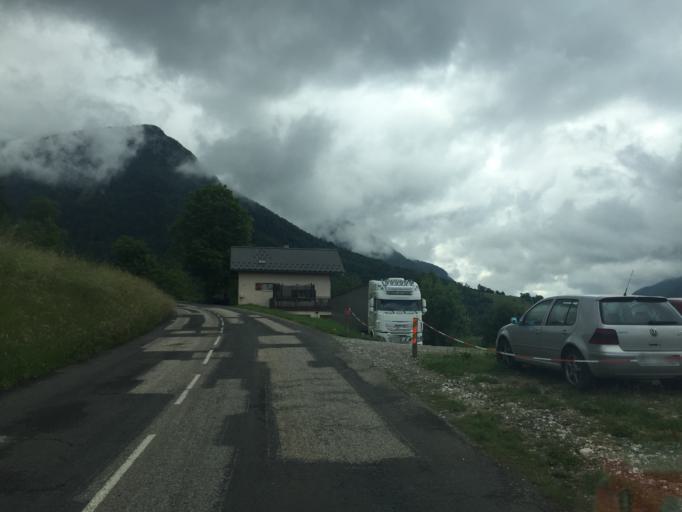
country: FR
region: Rhone-Alpes
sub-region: Departement de la Savoie
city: Barby
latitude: 45.5845
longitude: 6.0380
